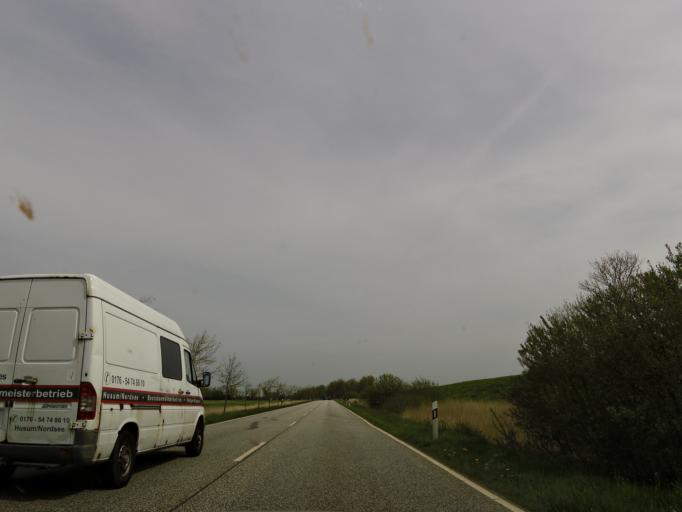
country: DE
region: Schleswig-Holstein
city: Witzwort
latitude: 54.3727
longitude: 8.9890
